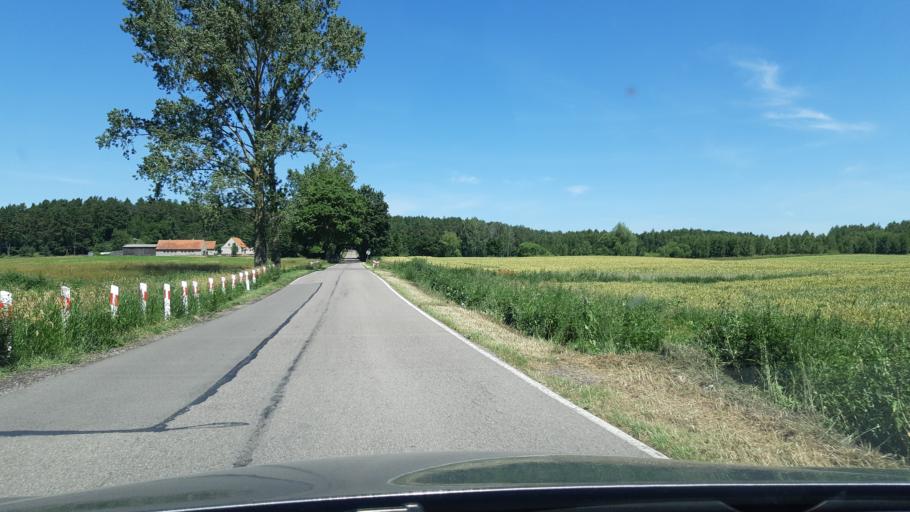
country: PL
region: Warmian-Masurian Voivodeship
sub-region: Powiat mragowski
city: Mikolajki
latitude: 53.8767
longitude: 21.6536
